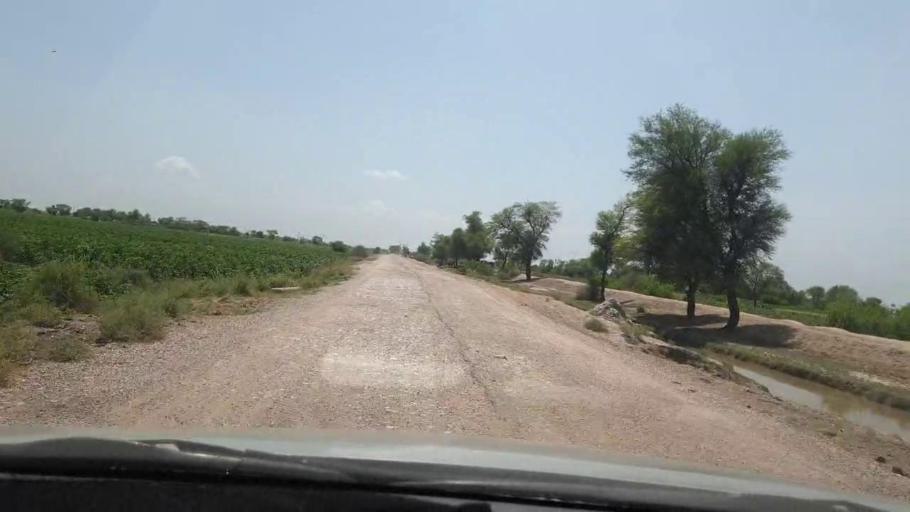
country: PK
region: Sindh
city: Pano Aqil
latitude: 27.7319
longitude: 69.1861
